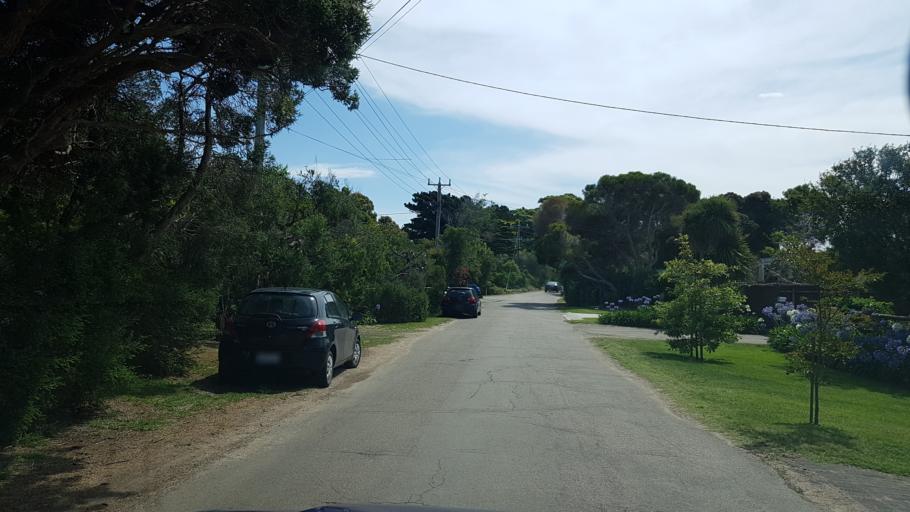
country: AU
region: Victoria
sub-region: Mornington Peninsula
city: Sorrento
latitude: -38.3240
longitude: 144.7149
